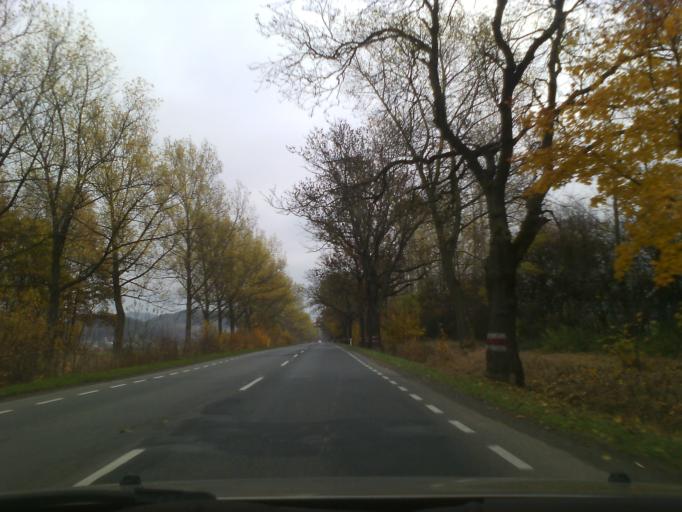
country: PL
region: Lower Silesian Voivodeship
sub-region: Powiat walbrzyski
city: Czarny Bor
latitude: 50.7761
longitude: 16.1150
